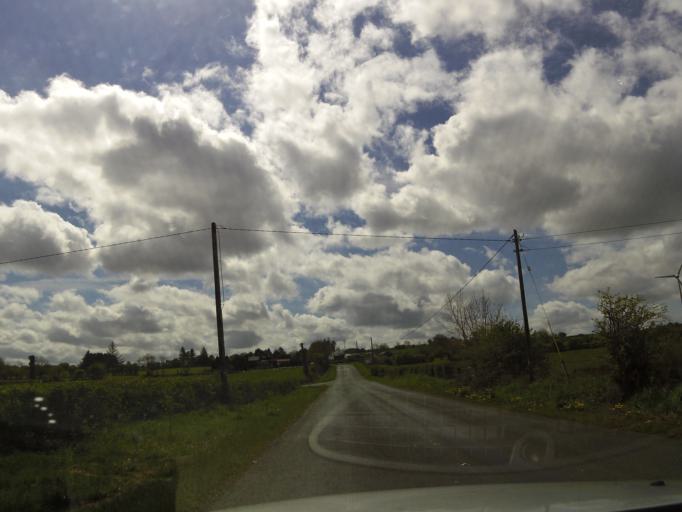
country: IE
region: Connaught
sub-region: Maigh Eo
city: Claremorris
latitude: 53.7734
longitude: -8.9603
